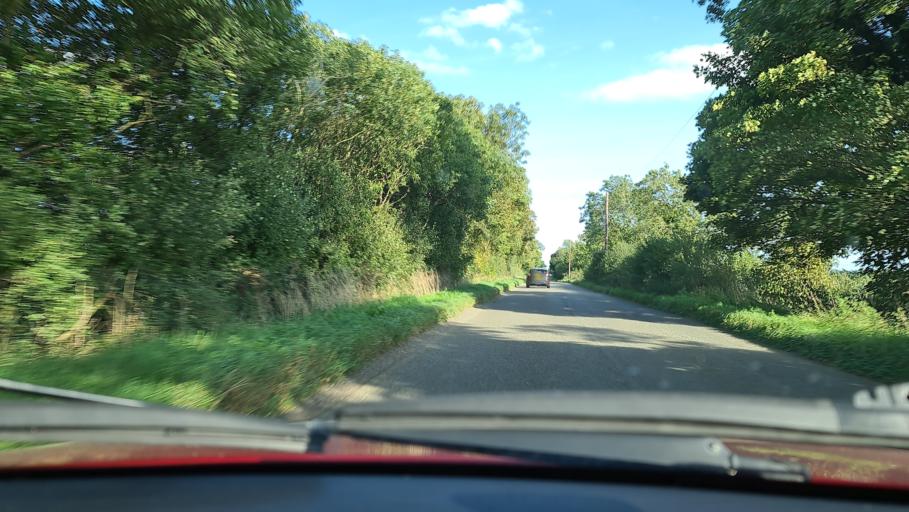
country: GB
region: England
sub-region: Northamptonshire
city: Brackley
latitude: 52.0159
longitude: -1.1810
